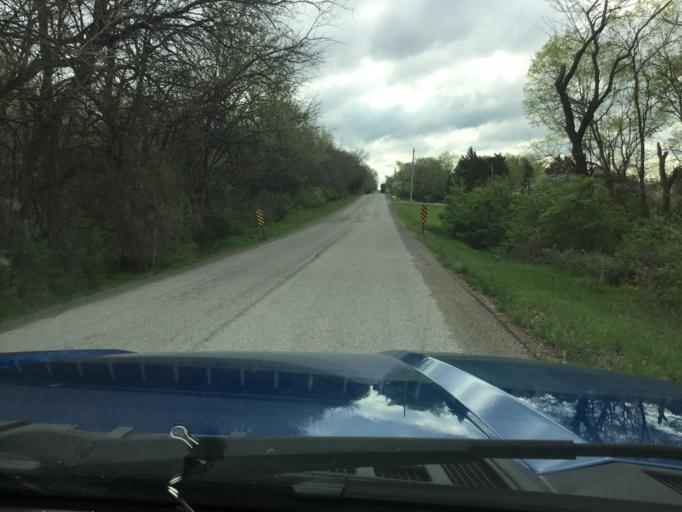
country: US
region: Kansas
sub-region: Douglas County
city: Lawrence
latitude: 38.9282
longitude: -95.2013
